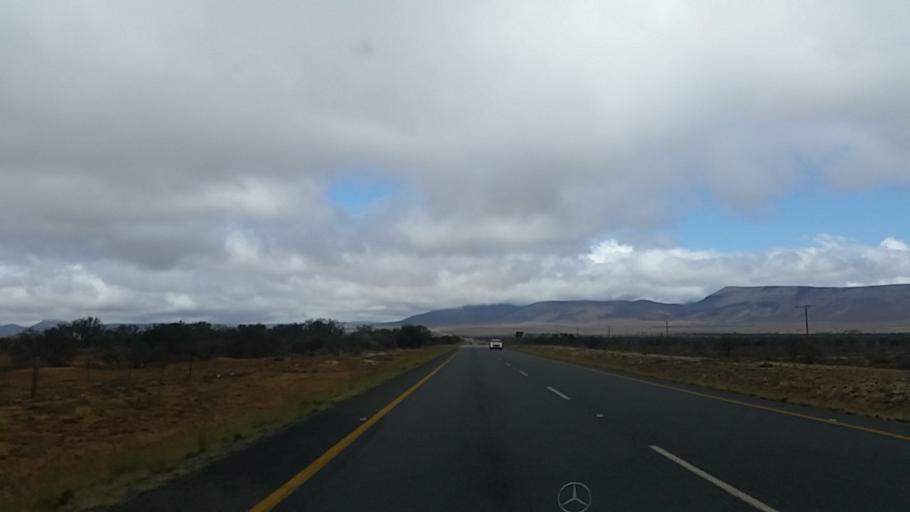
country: ZA
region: Eastern Cape
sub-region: Cacadu District Municipality
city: Graaff-Reinet
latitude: -31.9927
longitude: 24.6804
